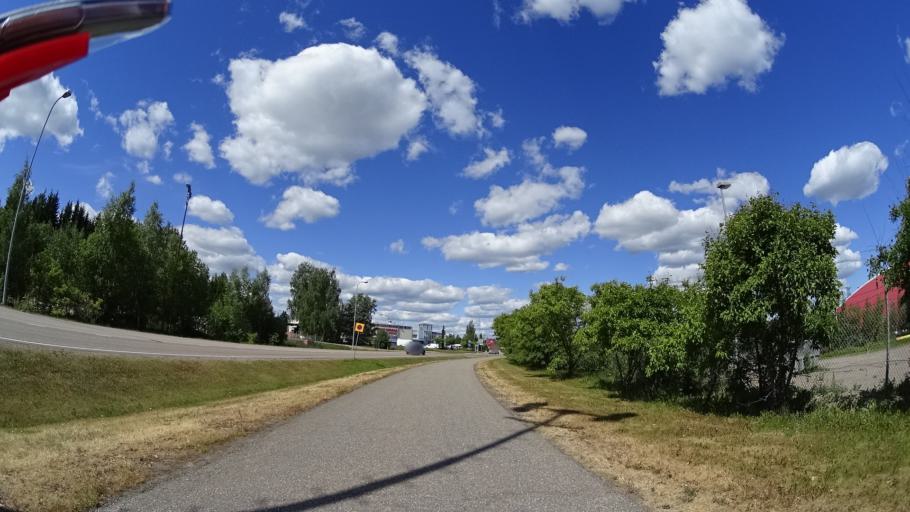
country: FI
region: Uusimaa
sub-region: Helsinki
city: Teekkarikylae
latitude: 60.2955
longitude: 24.8936
